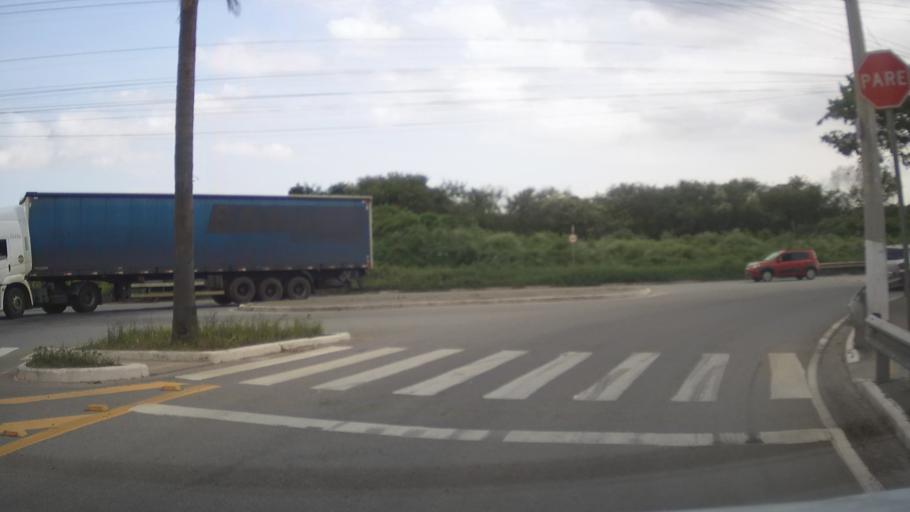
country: BR
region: Sao Paulo
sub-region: Guarulhos
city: Guarulhos
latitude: -23.4169
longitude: -46.4719
